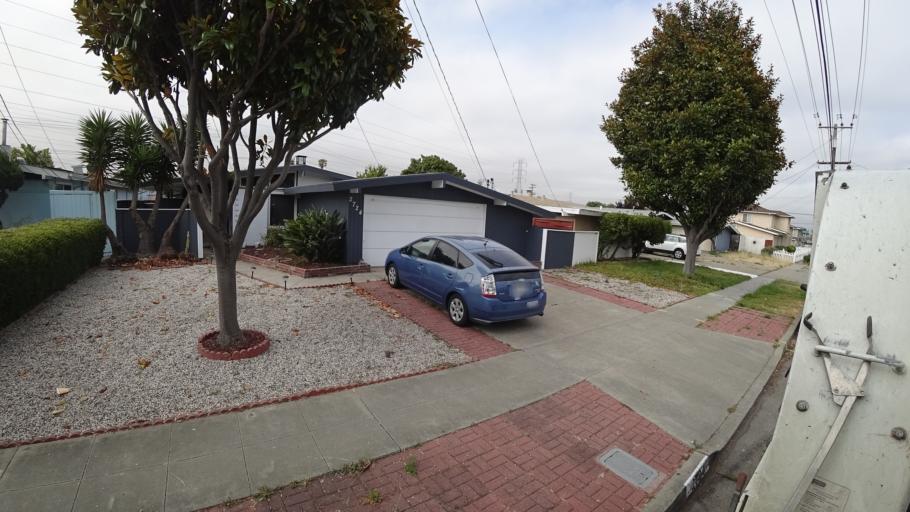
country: US
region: California
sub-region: Alameda County
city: Hayward
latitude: 37.6314
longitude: -122.1066
